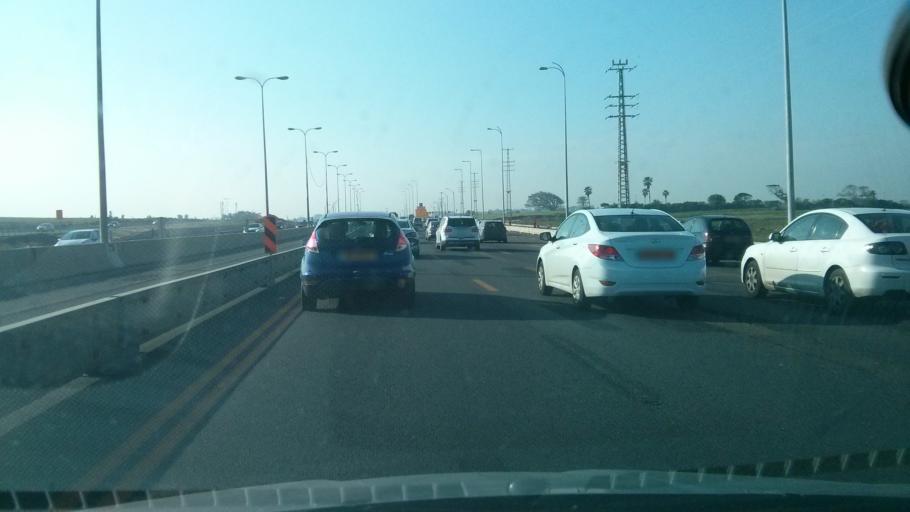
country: IL
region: Tel Aviv
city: Kefar Shemaryahu
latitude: 32.2384
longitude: 34.8332
